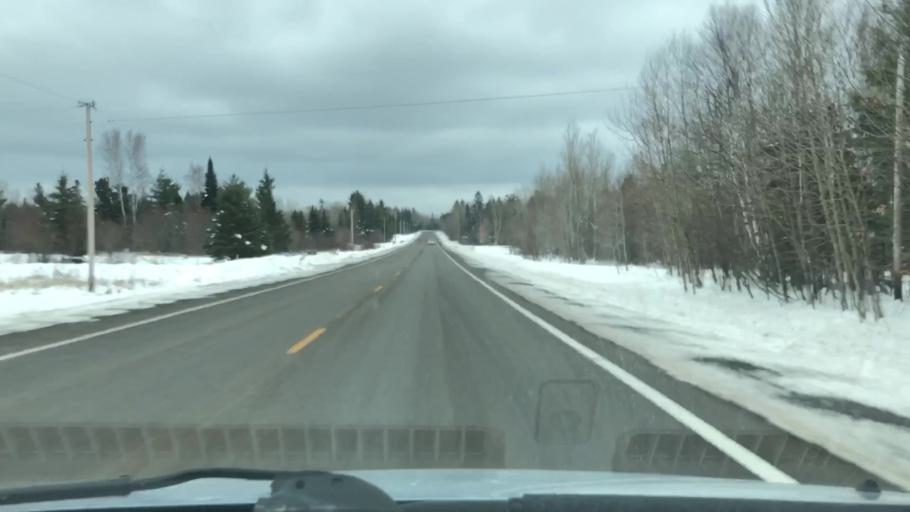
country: US
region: Minnesota
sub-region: Carlton County
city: Esko
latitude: 46.6916
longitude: -92.3649
